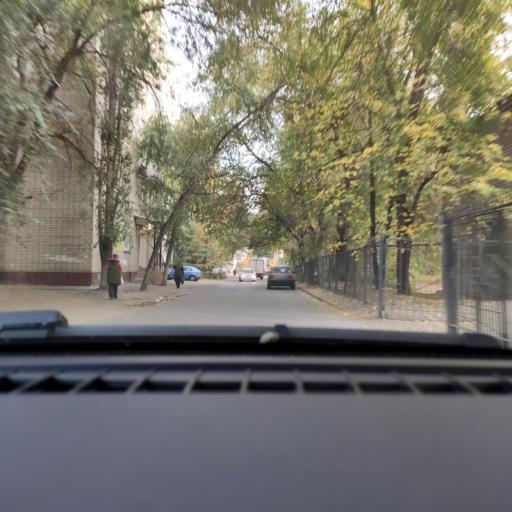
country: RU
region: Voronezj
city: Voronezh
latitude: 51.6419
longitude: 39.2707
